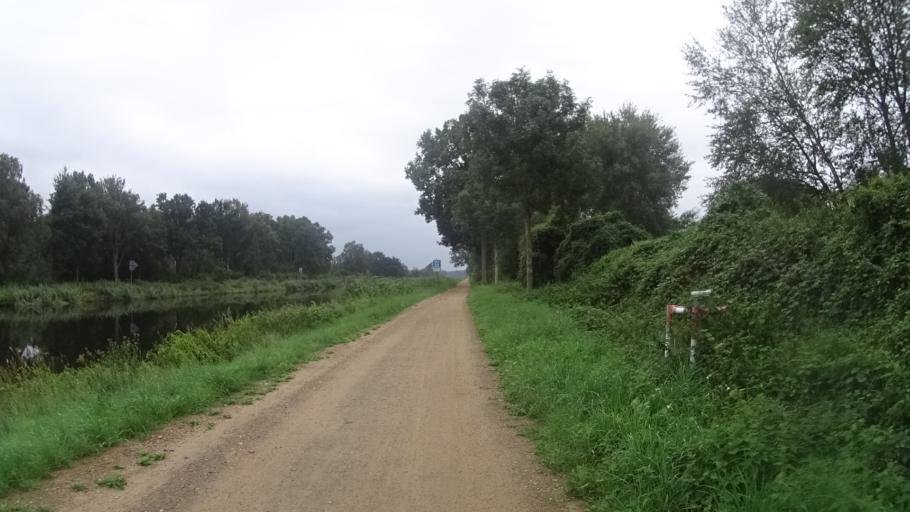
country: DE
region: Schleswig-Holstein
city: Witzeeze
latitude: 53.4487
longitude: 10.6214
